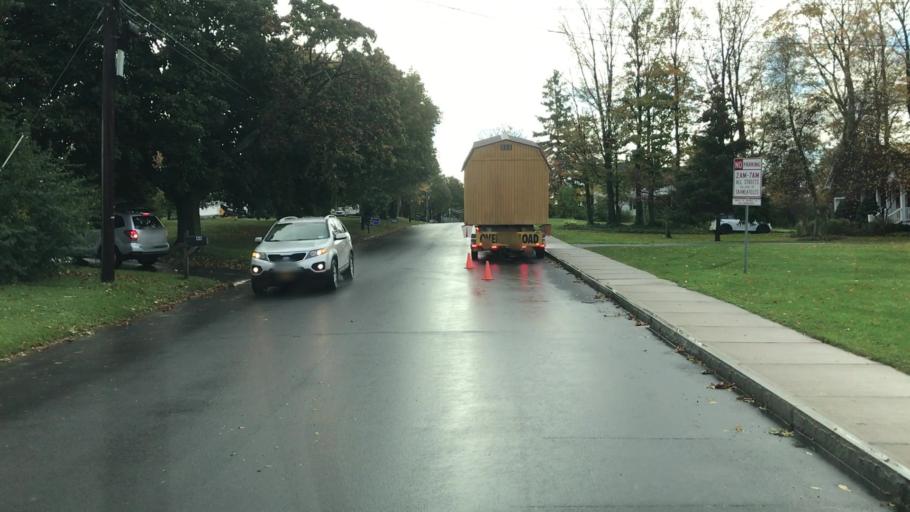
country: US
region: New York
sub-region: Onondaga County
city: Skaneateles
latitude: 42.9545
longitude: -76.4217
